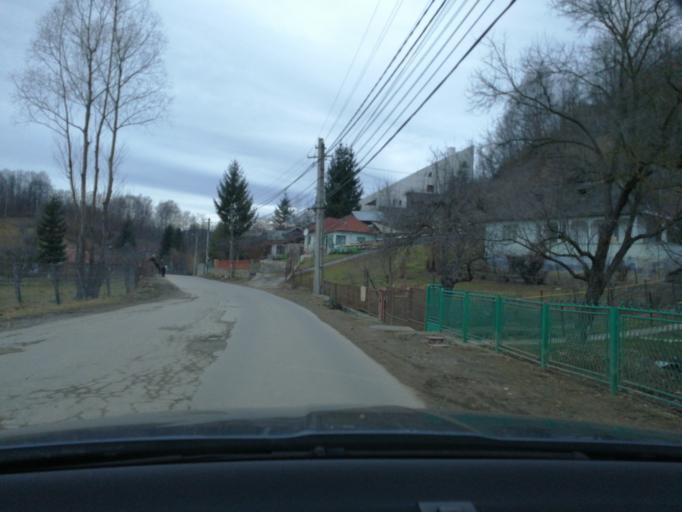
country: RO
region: Prahova
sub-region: Oras Breaza
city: Valea Tarsei
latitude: 45.1798
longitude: 25.6449
